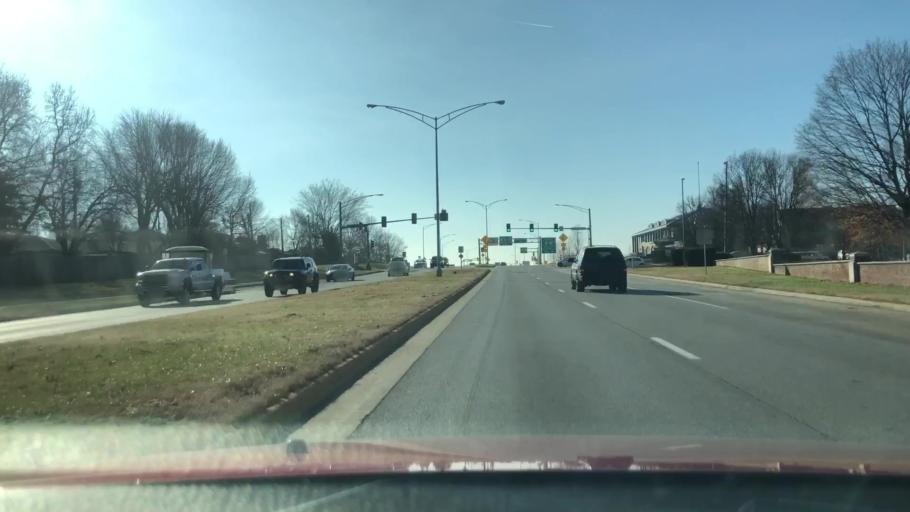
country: US
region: Missouri
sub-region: Greene County
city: Battlefield
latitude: 37.1470
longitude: -93.3193
